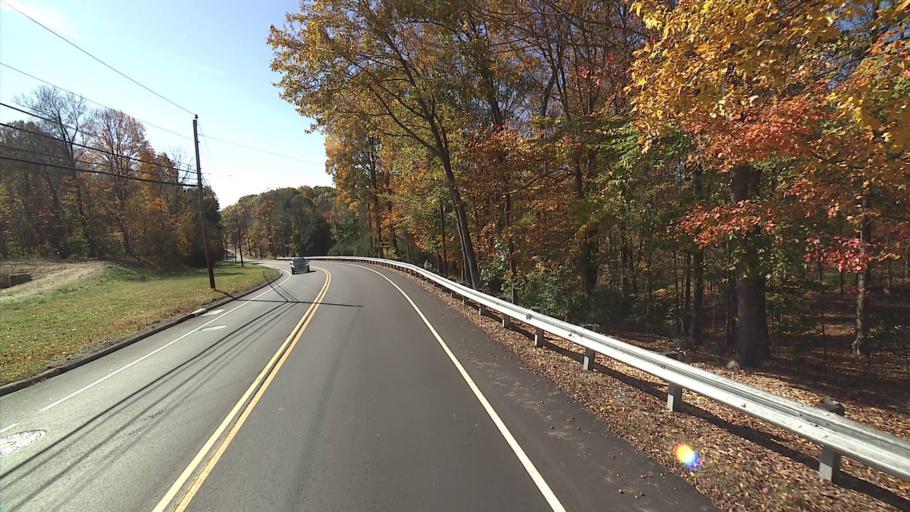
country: US
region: Connecticut
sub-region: Litchfield County
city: Watertown
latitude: 41.6190
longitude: -73.1101
